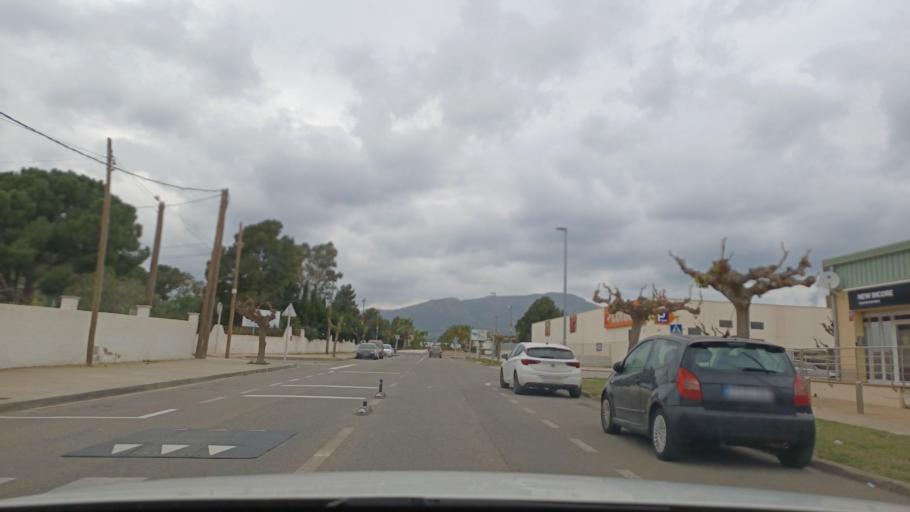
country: ES
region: Catalonia
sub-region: Provincia de Tarragona
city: Colldejou
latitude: 41.0183
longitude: 0.9409
